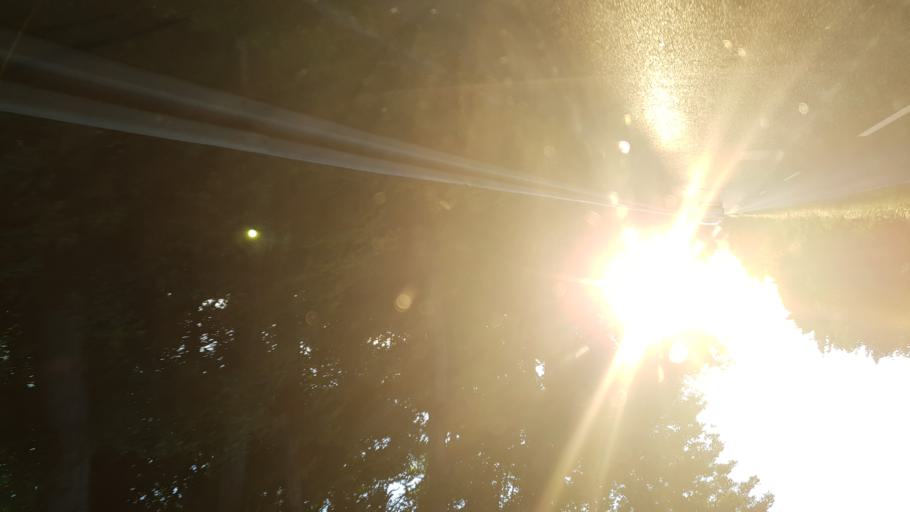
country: DE
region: Hesse
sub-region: Regierungsbezirk Darmstadt
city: Hofheim am Taunus
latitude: 50.0803
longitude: 8.4569
